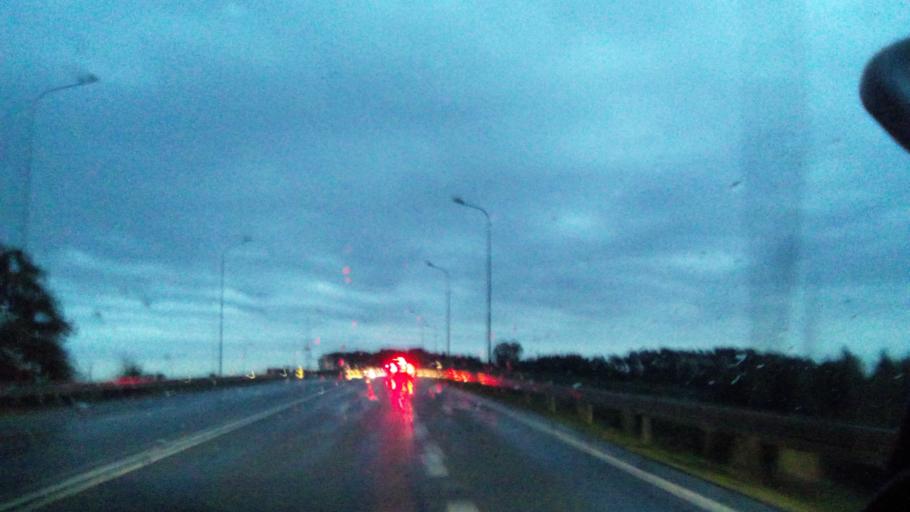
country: PL
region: Kujawsko-Pomorskie
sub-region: Powiat nakielski
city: Szubin
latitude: 53.0191
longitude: 17.7659
